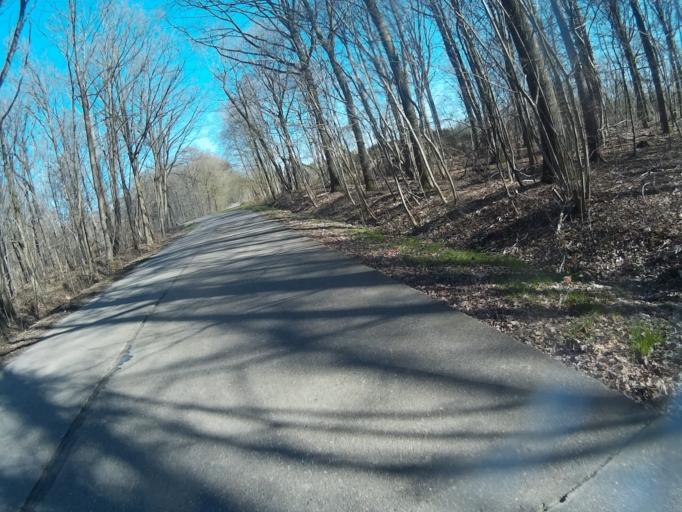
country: BE
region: Flanders
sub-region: Provincie Oost-Vlaanderen
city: Knesselare
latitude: 51.1417
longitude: 3.4533
